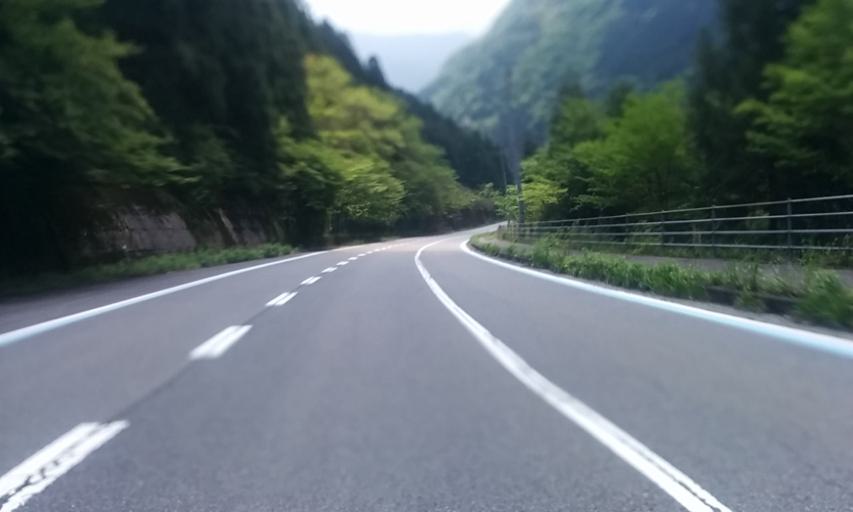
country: JP
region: Ehime
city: Saijo
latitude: 33.8174
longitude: 133.2324
